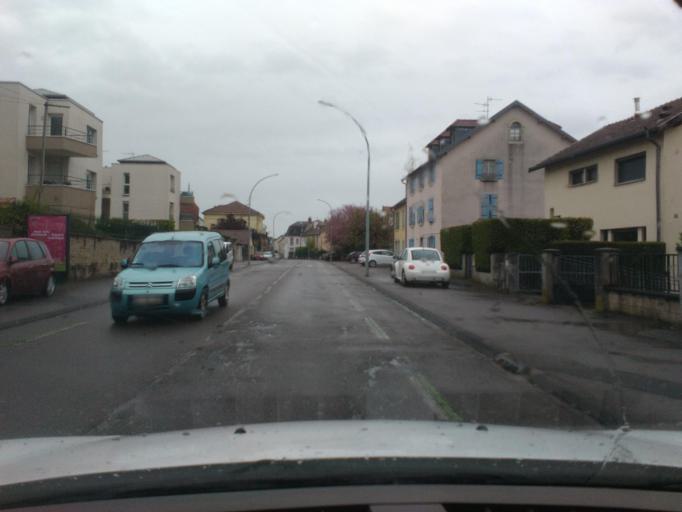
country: FR
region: Franche-Comte
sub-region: Departement de la Haute-Saone
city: Vesoul
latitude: 47.6260
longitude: 6.1653
